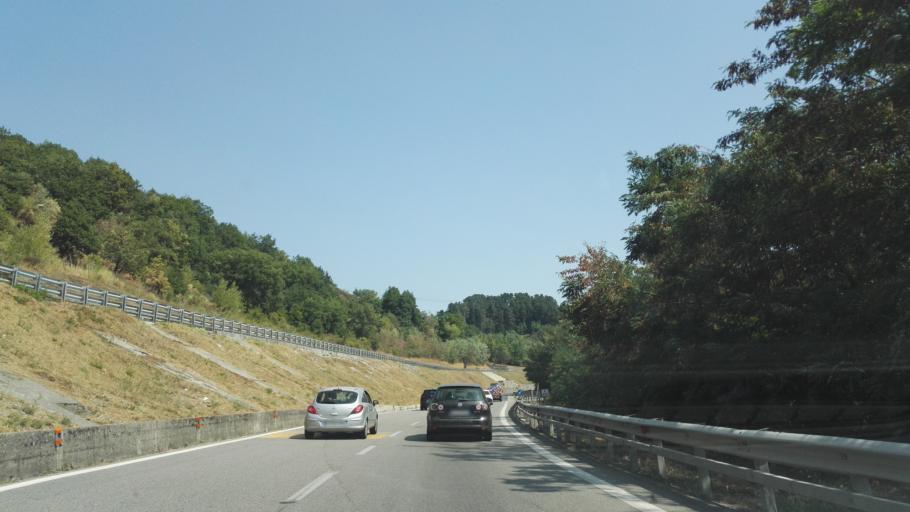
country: IT
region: Calabria
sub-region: Provincia di Cosenza
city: Belsito
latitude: 39.1595
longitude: 16.2868
